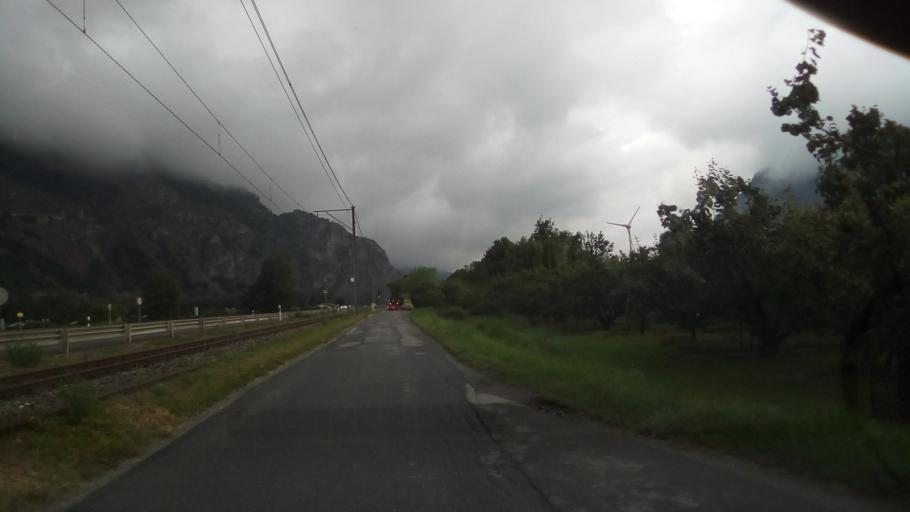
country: CH
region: Valais
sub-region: Martigny District
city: Martigny-Ville
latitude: 46.1169
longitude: 7.0559
